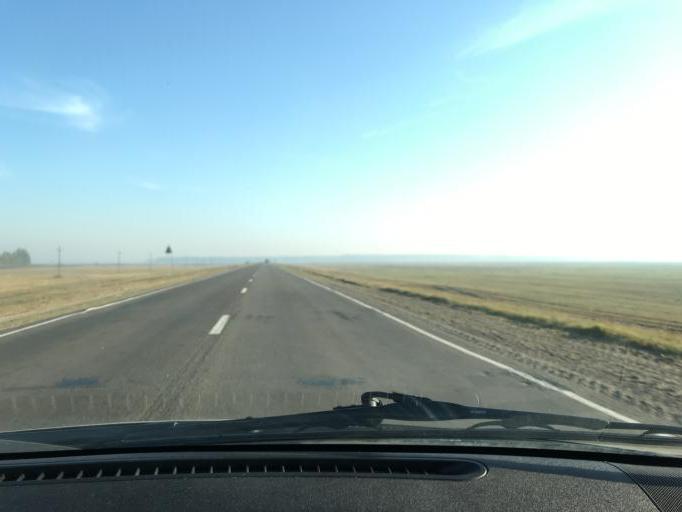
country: BY
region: Brest
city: Asnyezhytsy
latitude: 52.2811
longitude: 26.4033
